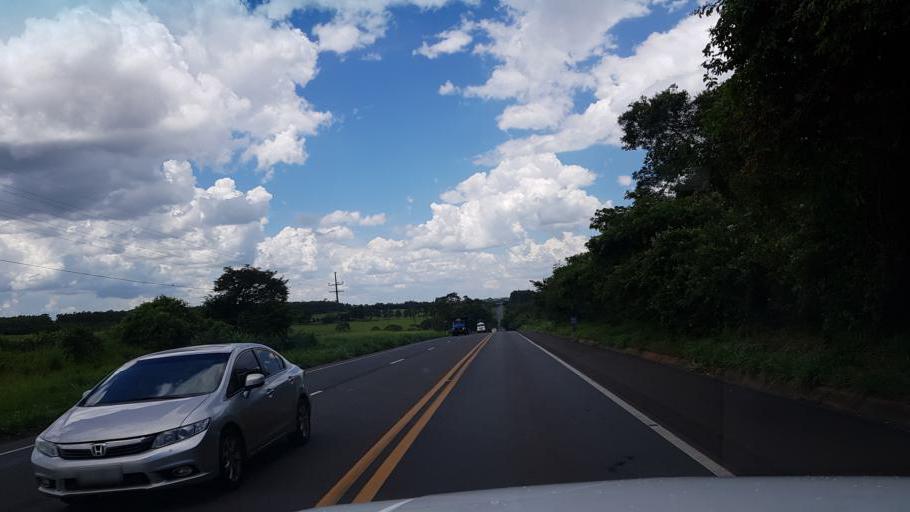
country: BR
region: Sao Paulo
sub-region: Paraguacu Paulista
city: Paraguacu Paulista
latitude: -22.3886
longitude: -50.6129
